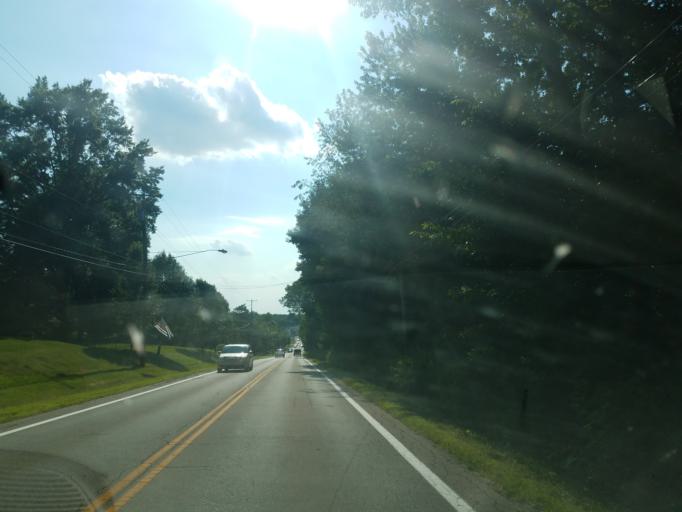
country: US
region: Ohio
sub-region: Stark County
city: Uniontown
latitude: 40.9763
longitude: -81.4009
